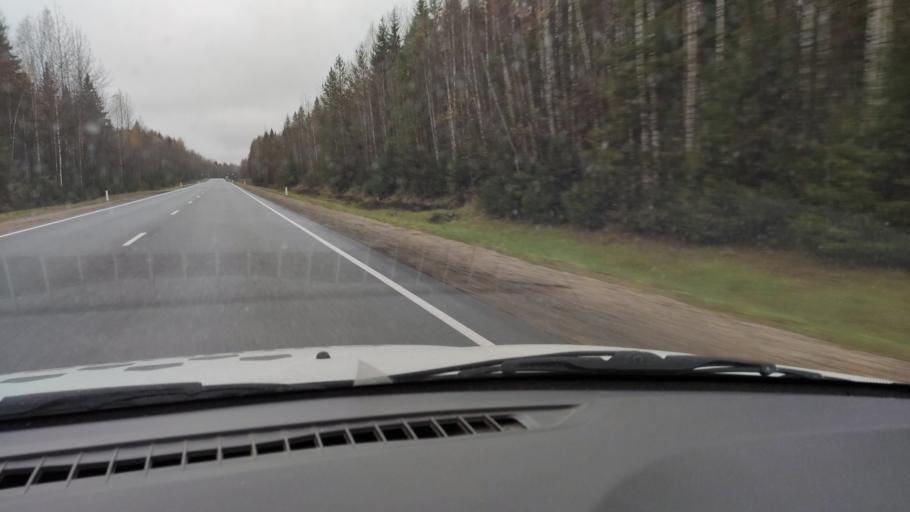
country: RU
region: Kirov
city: Chernaya Kholunitsa
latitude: 58.7743
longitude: 51.9366
